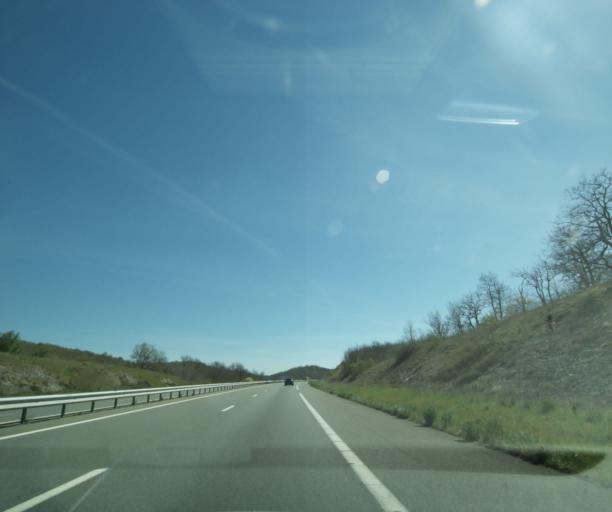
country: FR
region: Midi-Pyrenees
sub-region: Departement du Lot
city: Le Vigan
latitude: 44.7733
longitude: 1.5374
